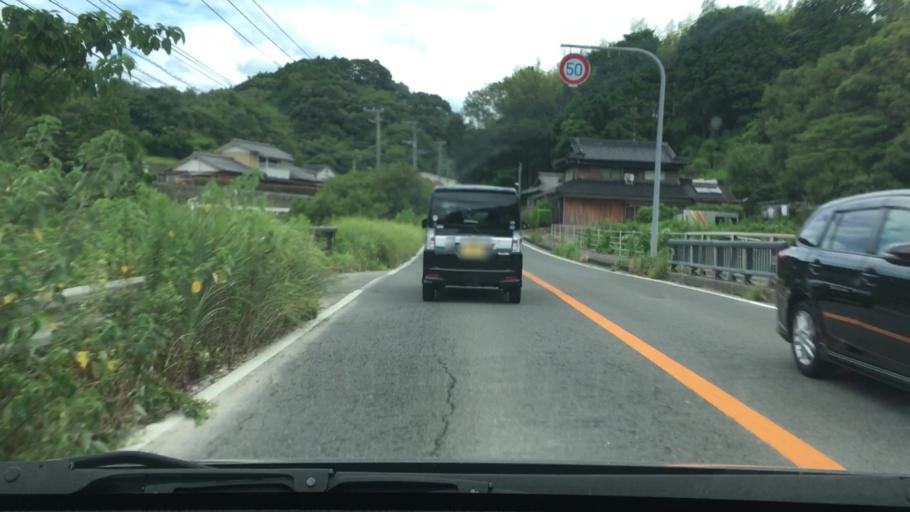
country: JP
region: Nagasaki
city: Togitsu
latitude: 32.9836
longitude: 129.7796
